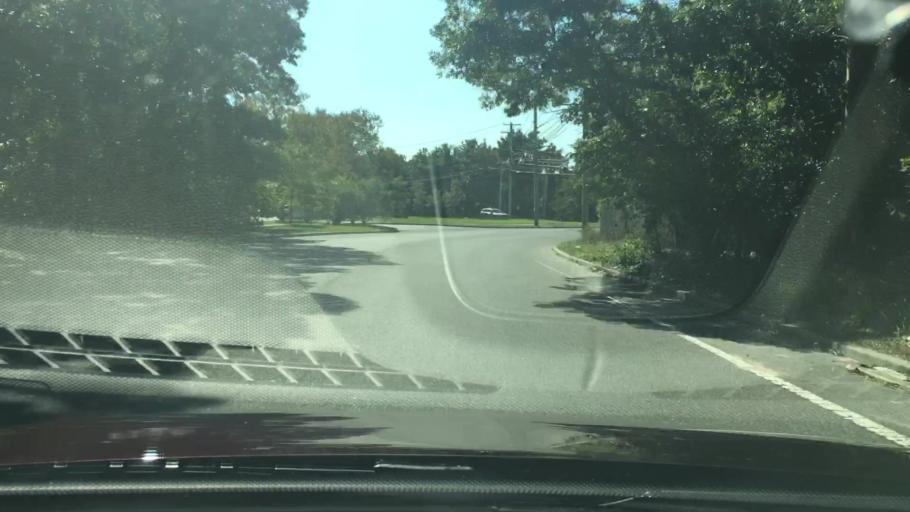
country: US
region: New York
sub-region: Suffolk County
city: Holtsville
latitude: 40.7982
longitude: -73.0423
